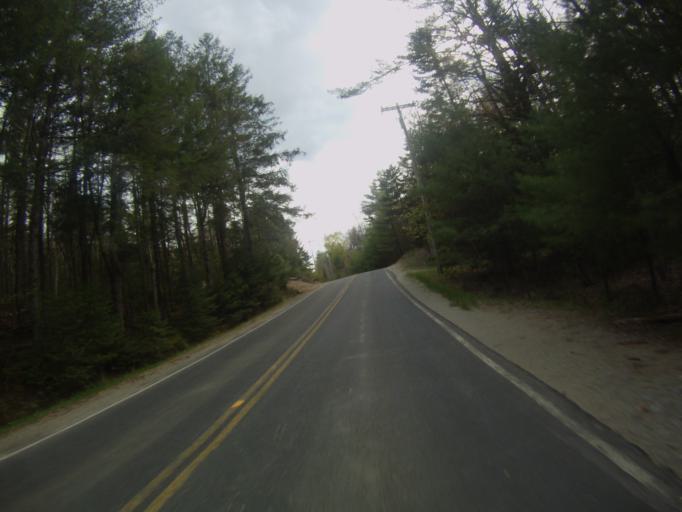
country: US
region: New York
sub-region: Warren County
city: Warrensburg
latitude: 43.8227
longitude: -73.9258
